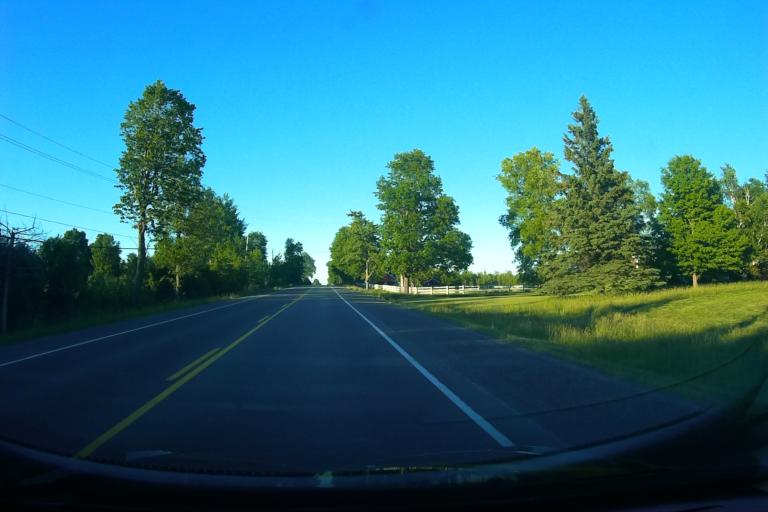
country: CA
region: Ontario
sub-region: Lanark County
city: Smiths Falls
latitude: 44.9861
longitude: -75.7202
